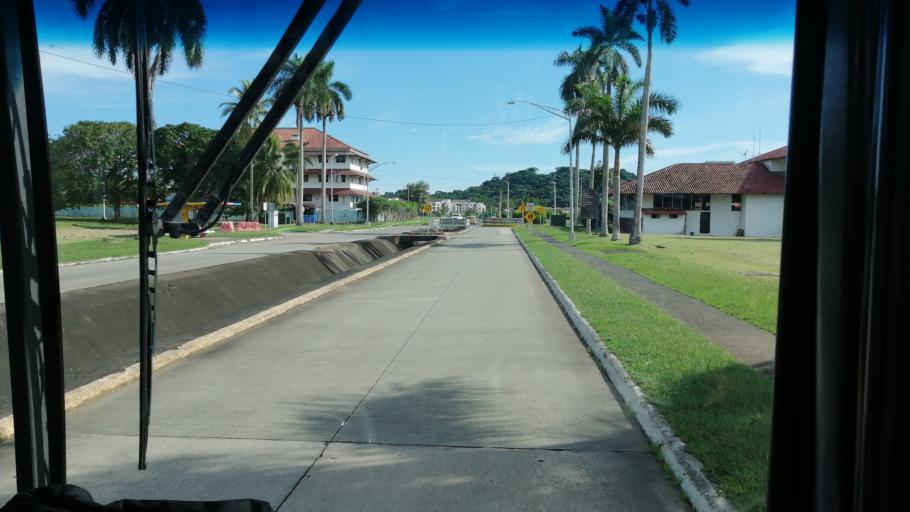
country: PA
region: Panama
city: Veracruz
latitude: 8.9121
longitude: -79.5920
